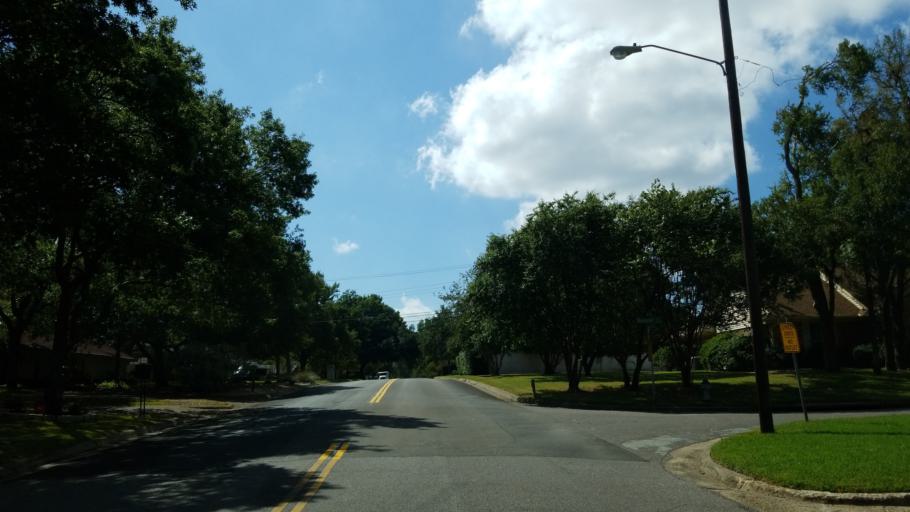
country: US
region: Texas
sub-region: Dallas County
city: Addison
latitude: 32.9312
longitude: -96.7975
